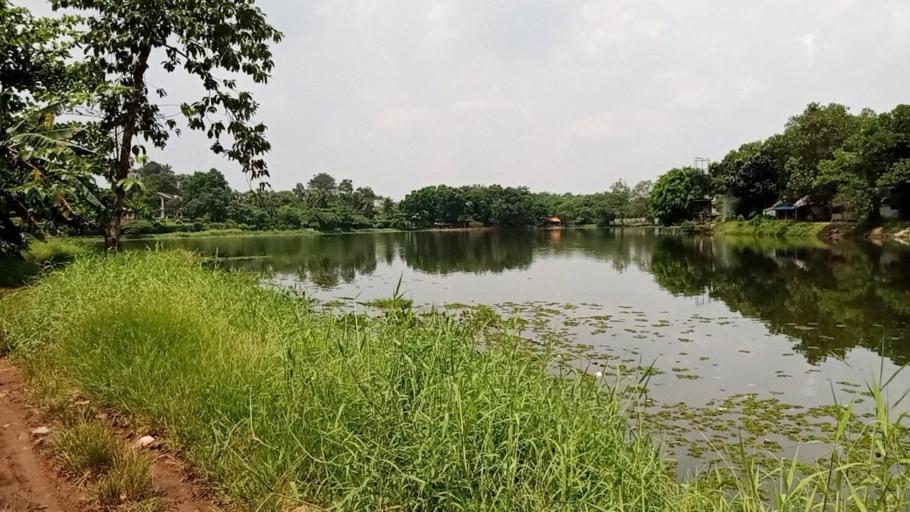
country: ID
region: West Java
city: Sawangan
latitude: -6.3856
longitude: 106.7552
